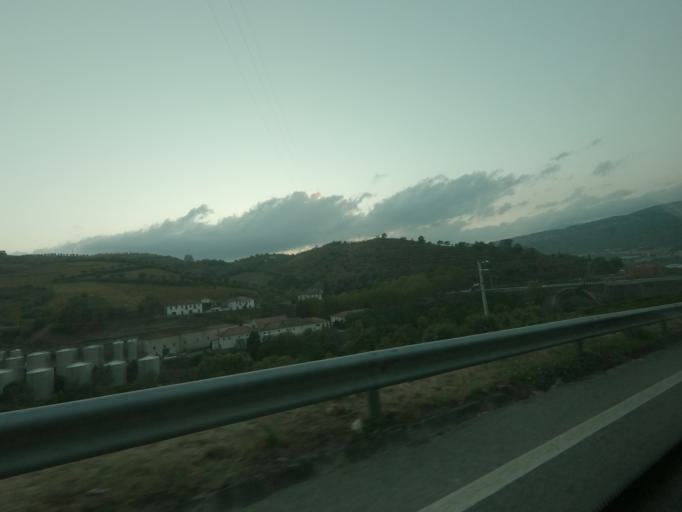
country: PT
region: Vila Real
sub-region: Peso da Regua
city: Peso da Regua
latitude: 41.1508
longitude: -7.7807
